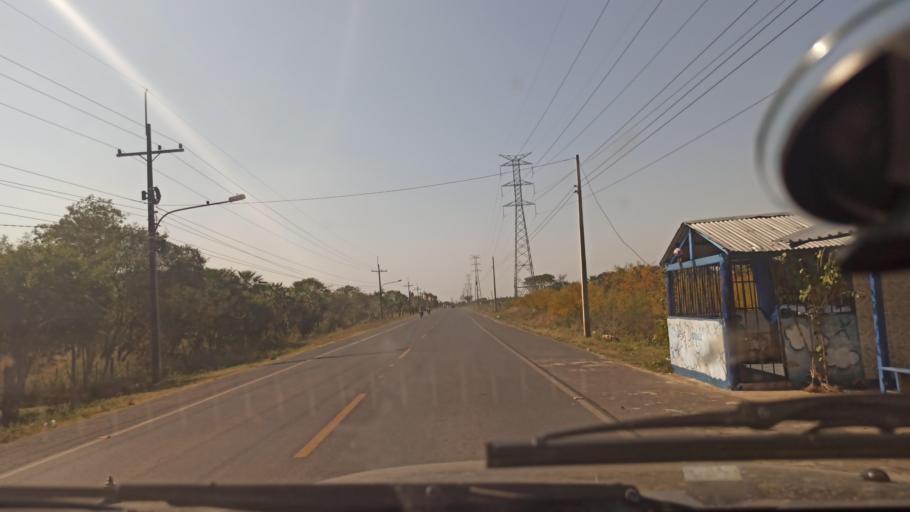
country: PY
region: Presidente Hayes
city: Nanawa
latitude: -25.2627
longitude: -57.6844
